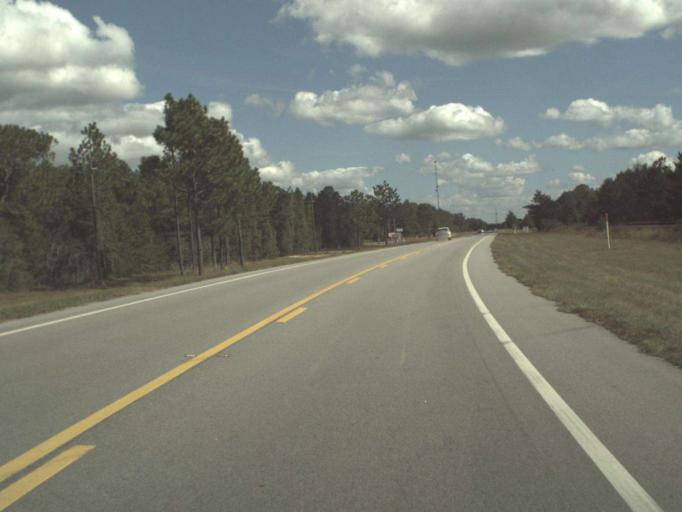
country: US
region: Florida
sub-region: Okaloosa County
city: Crestview
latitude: 30.7430
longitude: -86.3778
